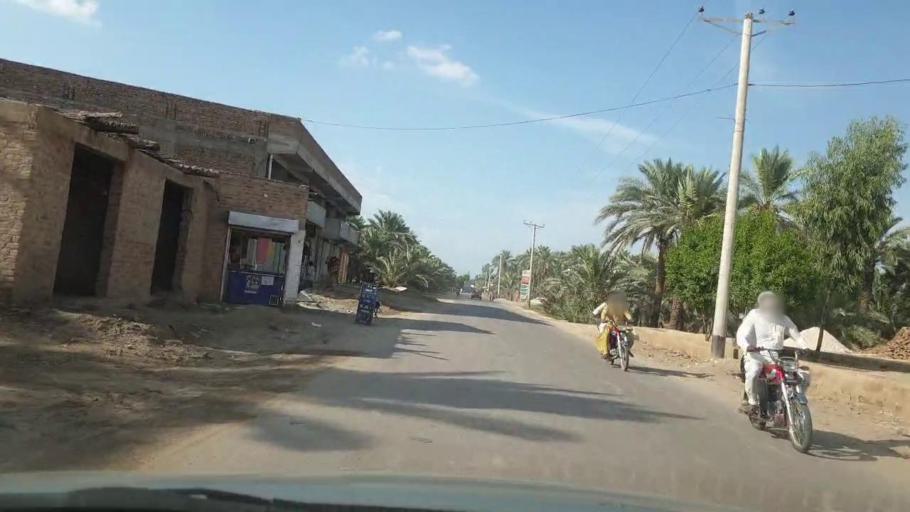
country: PK
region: Sindh
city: Sukkur
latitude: 27.6587
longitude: 68.8419
